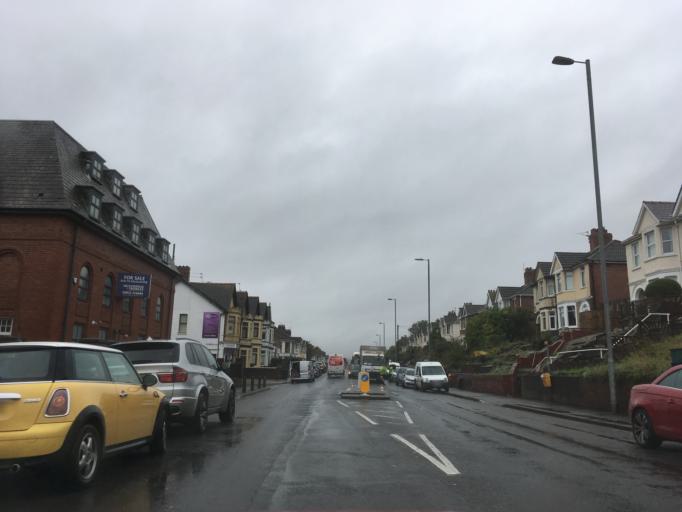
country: GB
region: Wales
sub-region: Newport
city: Caerleon
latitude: 51.5882
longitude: -2.9677
